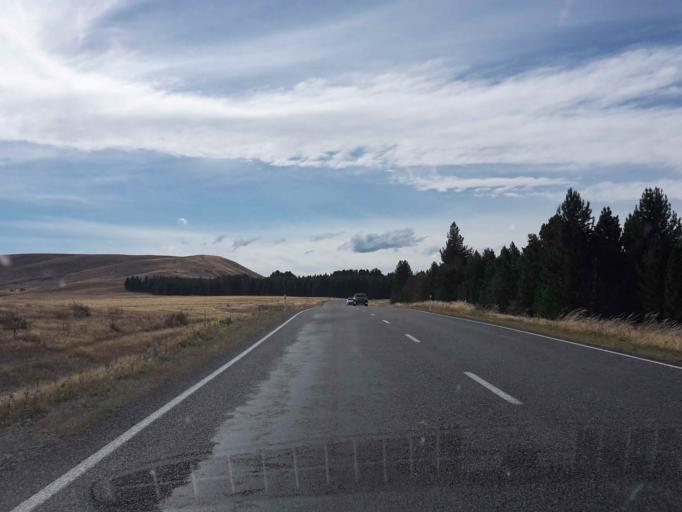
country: NZ
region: Canterbury
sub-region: Timaru District
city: Pleasant Point
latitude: -44.0182
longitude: 170.4033
